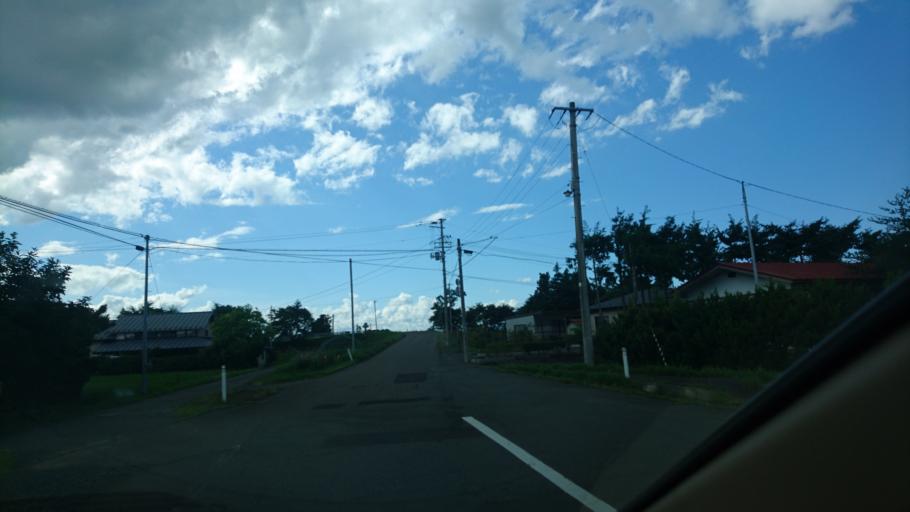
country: JP
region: Iwate
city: Mizusawa
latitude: 39.1939
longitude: 141.1621
